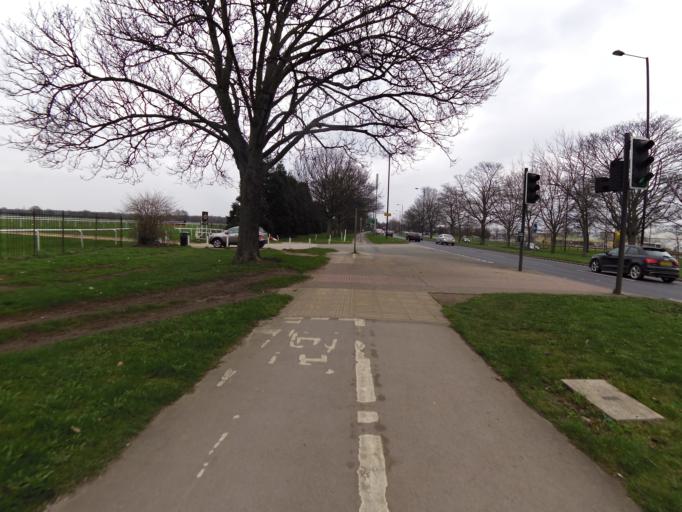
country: GB
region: England
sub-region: Doncaster
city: Doncaster
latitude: 53.5183
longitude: -1.1040
